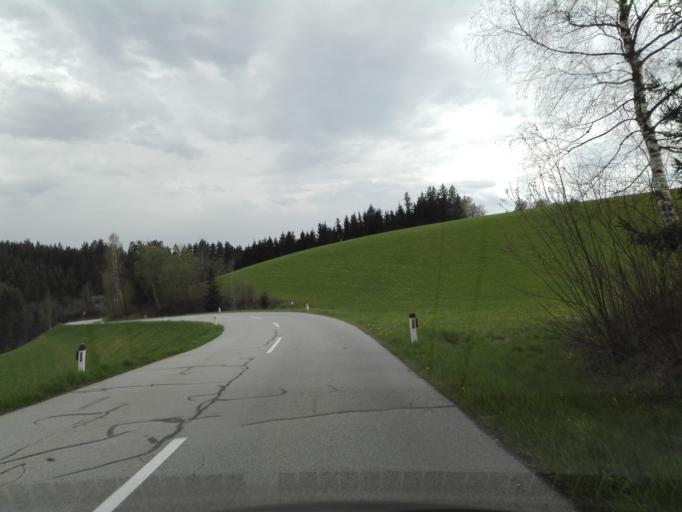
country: AT
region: Upper Austria
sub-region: Politischer Bezirk Rohrbach
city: Atzesberg
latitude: 48.5441
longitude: 13.9520
